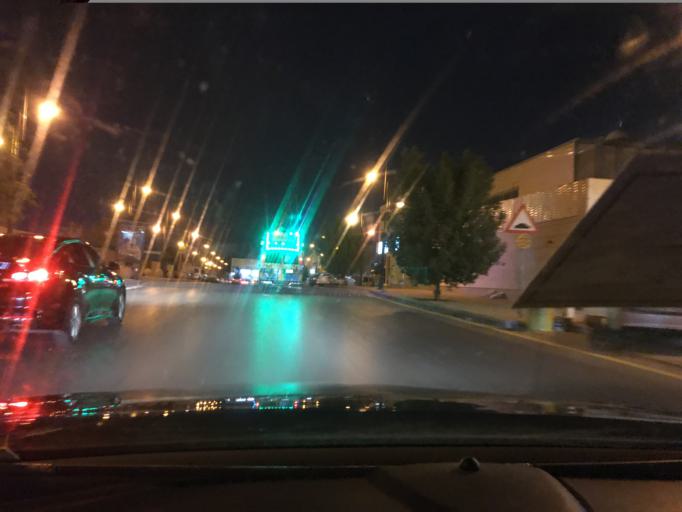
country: SA
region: Ar Riyad
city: Riyadh
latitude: 24.7427
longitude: 46.7688
